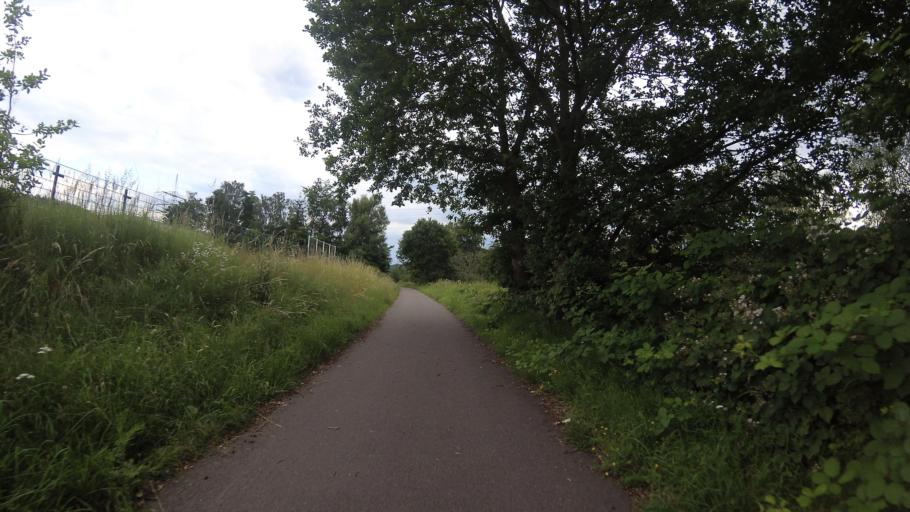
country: DE
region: Saarland
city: Homburg
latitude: 49.3049
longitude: 7.3244
